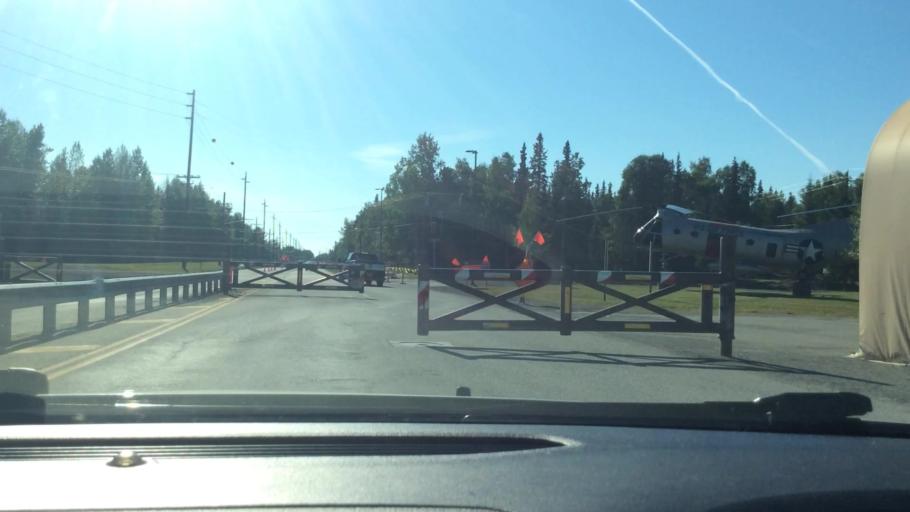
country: US
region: Alaska
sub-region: Anchorage Municipality
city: Elmendorf Air Force Base
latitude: 61.2314
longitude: -149.7472
